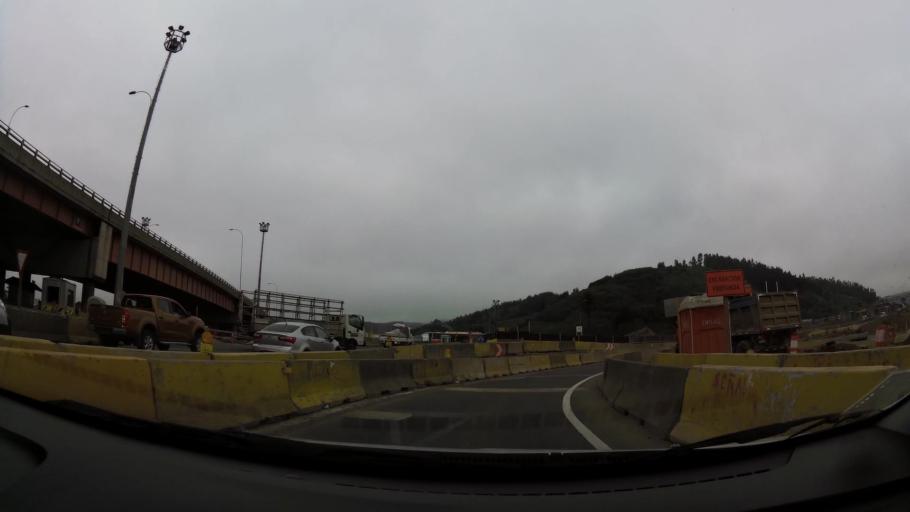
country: CL
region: Biobio
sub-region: Provincia de Concepcion
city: Concepcion
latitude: -36.8114
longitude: -73.0276
